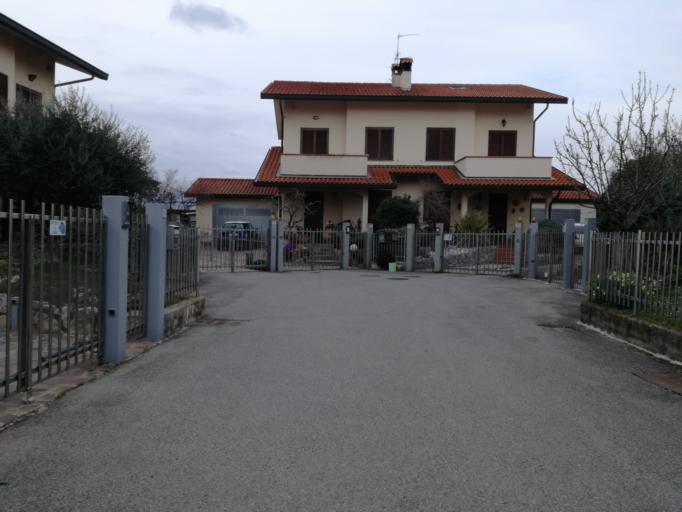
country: IT
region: Lombardy
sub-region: Provincia di Lecco
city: Verderio Superiore
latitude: 45.6659
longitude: 9.4462
